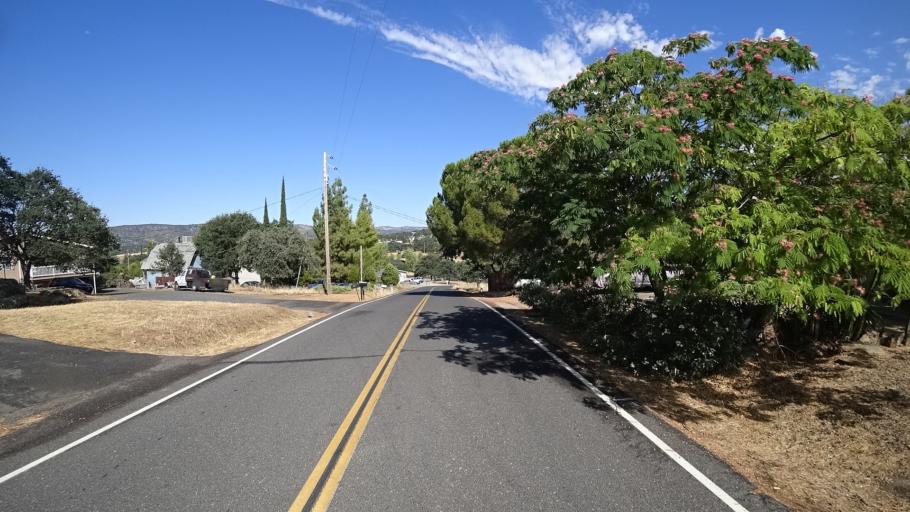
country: US
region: California
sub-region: Calaveras County
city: Copperopolis
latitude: 37.9156
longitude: -120.6148
